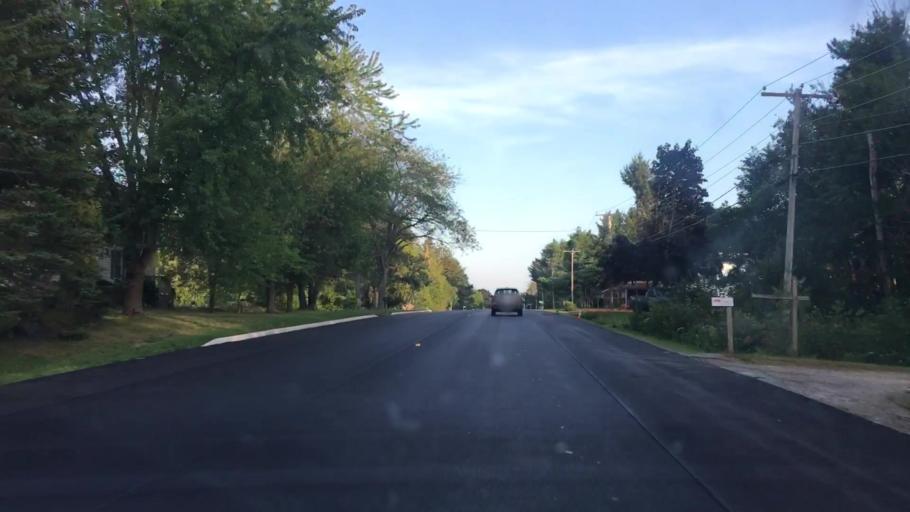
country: US
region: Maine
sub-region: Penobscot County
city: Hampden
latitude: 44.7636
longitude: -68.8508
